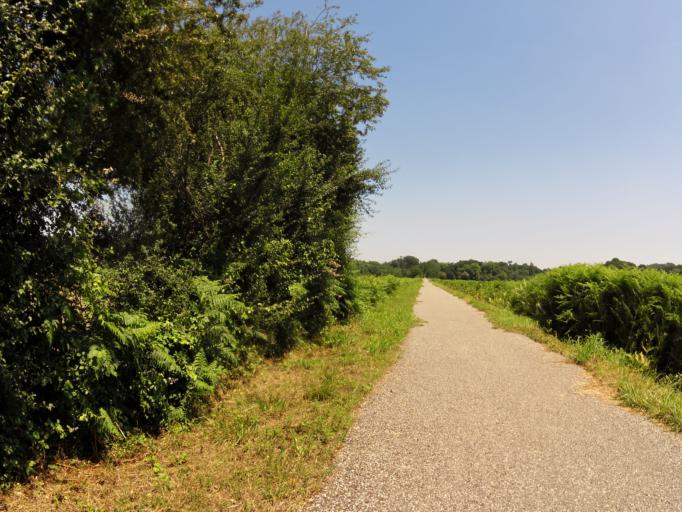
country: FR
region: Aquitaine
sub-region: Departement des Pyrenees-Atlantiques
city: Salies-de-Bearn
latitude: 43.4585
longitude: -0.9860
